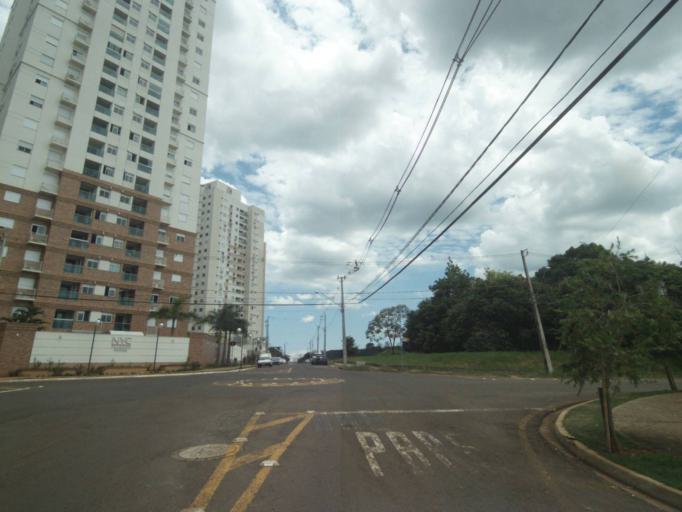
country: BR
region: Parana
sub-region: Londrina
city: Londrina
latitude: -23.3324
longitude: -51.1835
